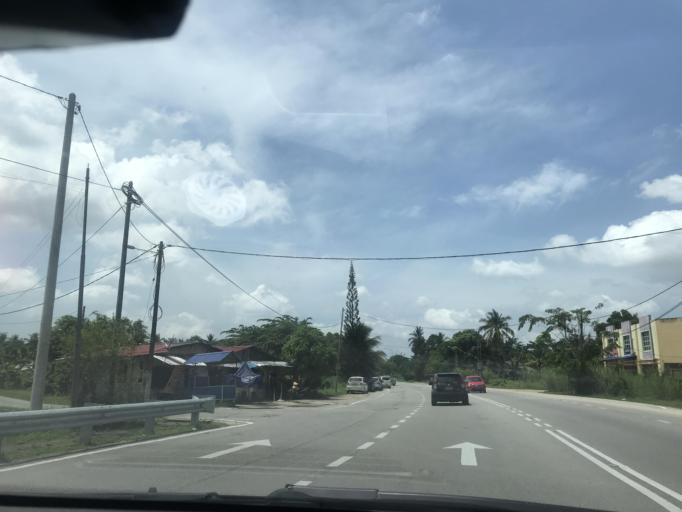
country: MY
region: Kelantan
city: Kota Bharu
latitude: 6.1546
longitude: 102.2033
